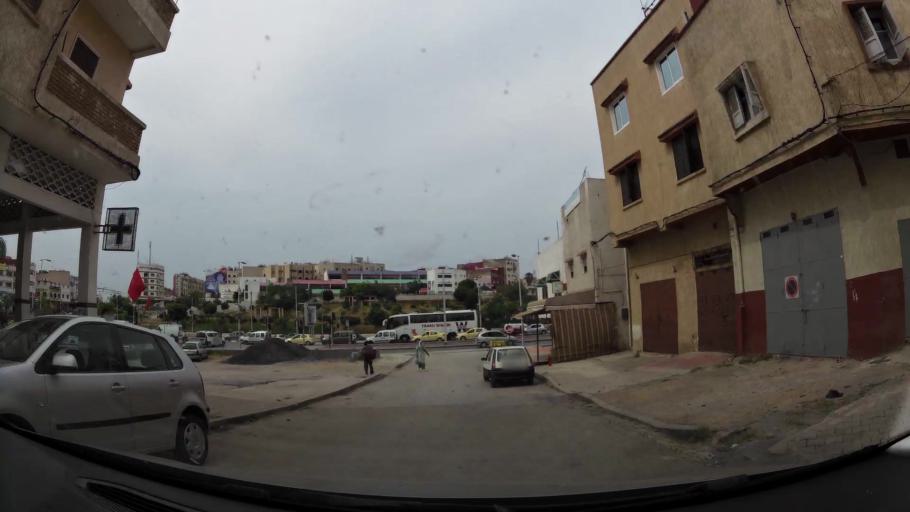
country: MA
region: Rabat-Sale-Zemmour-Zaer
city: Sale
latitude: 34.0344
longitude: -6.8051
